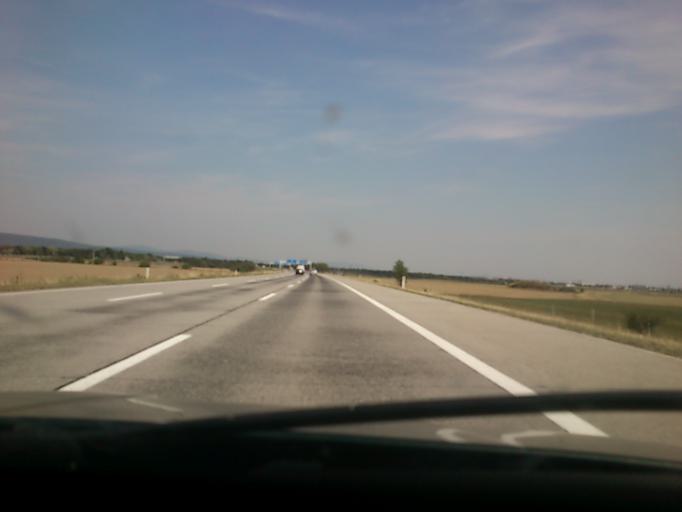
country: AT
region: Lower Austria
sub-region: Politischer Bezirk Wiener Neustadt
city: Bad Erlach
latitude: 47.7747
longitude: 16.2061
